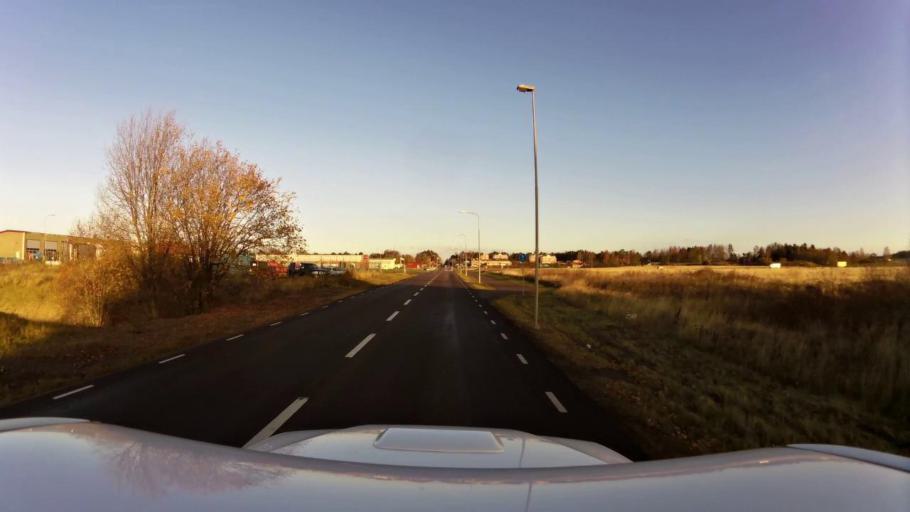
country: SE
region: OEstergoetland
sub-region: Linkopings Kommun
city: Linkoping
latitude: 58.4212
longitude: 15.6795
